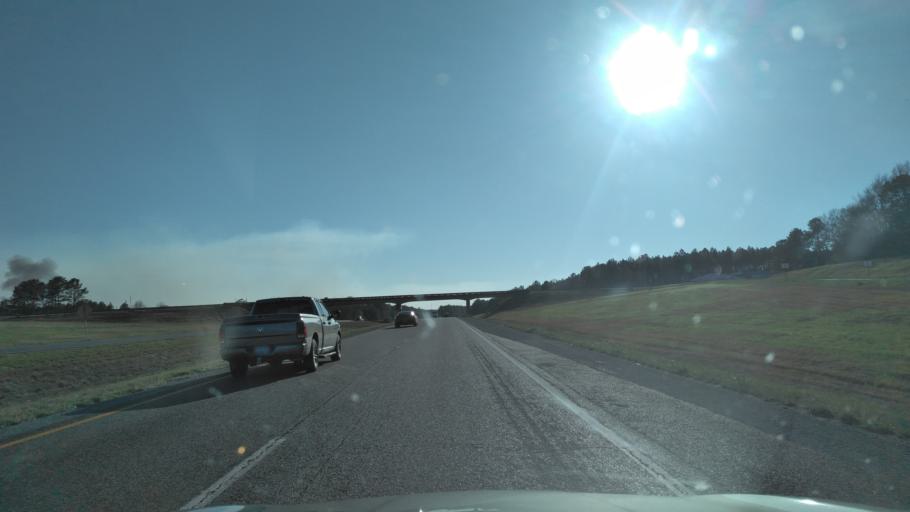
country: US
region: Alabama
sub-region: Escambia County
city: Atmore
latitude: 31.0208
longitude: -87.6539
